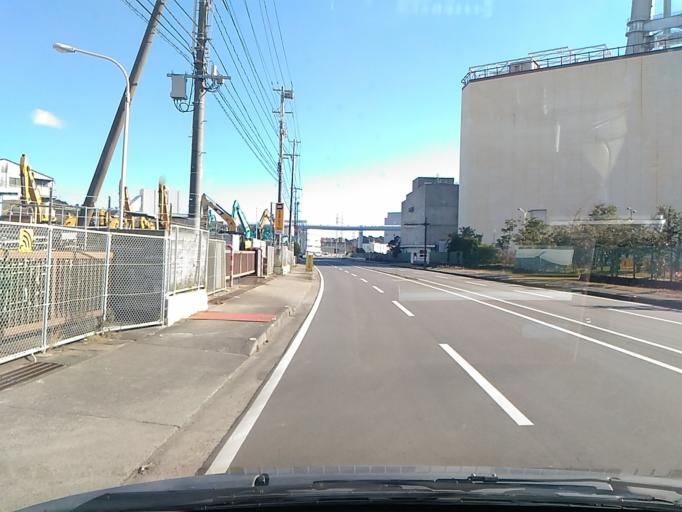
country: JP
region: Ibaraki
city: Kitaibaraki
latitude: 36.9144
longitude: 140.8108
